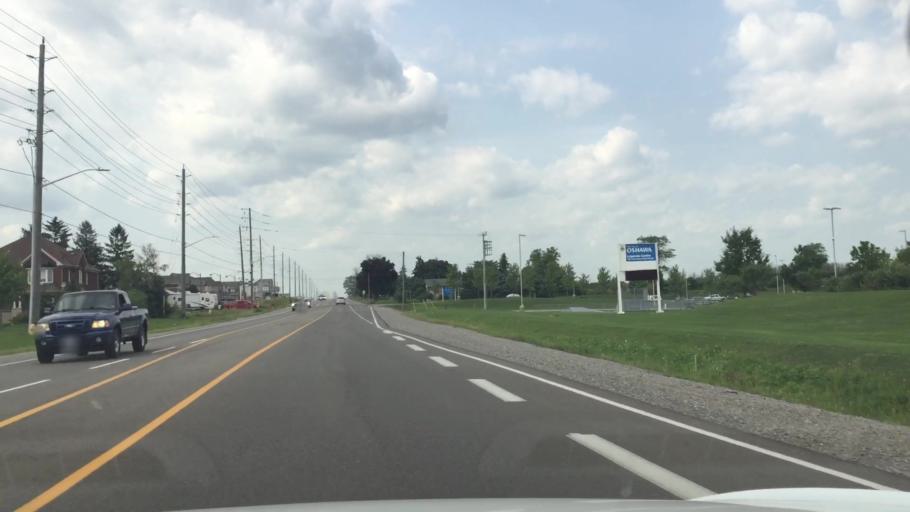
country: CA
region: Ontario
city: Oshawa
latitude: 43.9472
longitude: -78.8528
